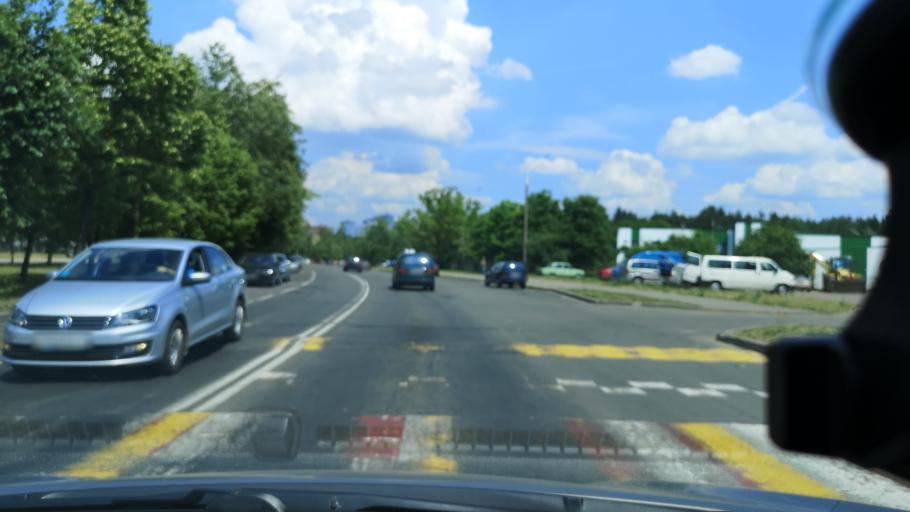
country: BY
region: Minsk
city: Lyeskawka
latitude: 53.9395
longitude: 27.6942
